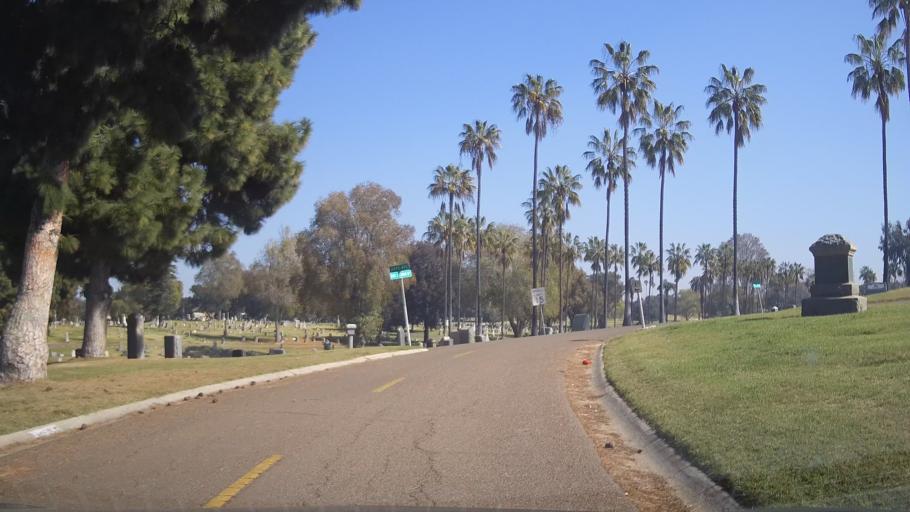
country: US
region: California
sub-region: San Diego County
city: National City
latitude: 32.7054
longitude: -117.1117
